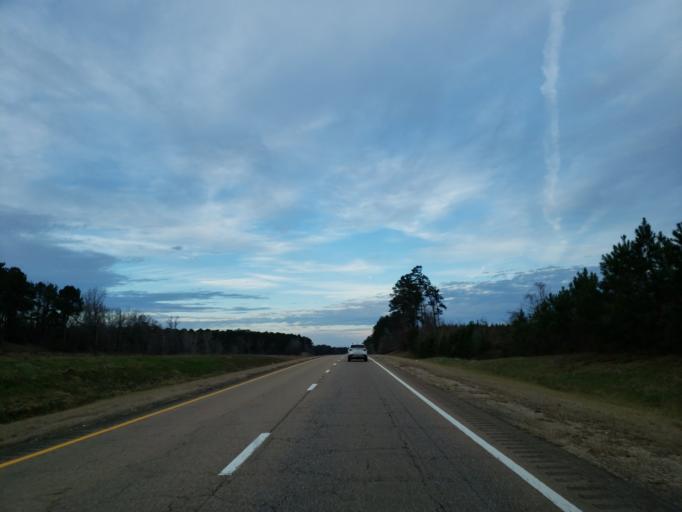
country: US
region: Mississippi
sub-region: Lauderdale County
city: Meridian Station
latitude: 32.4793
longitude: -88.5993
